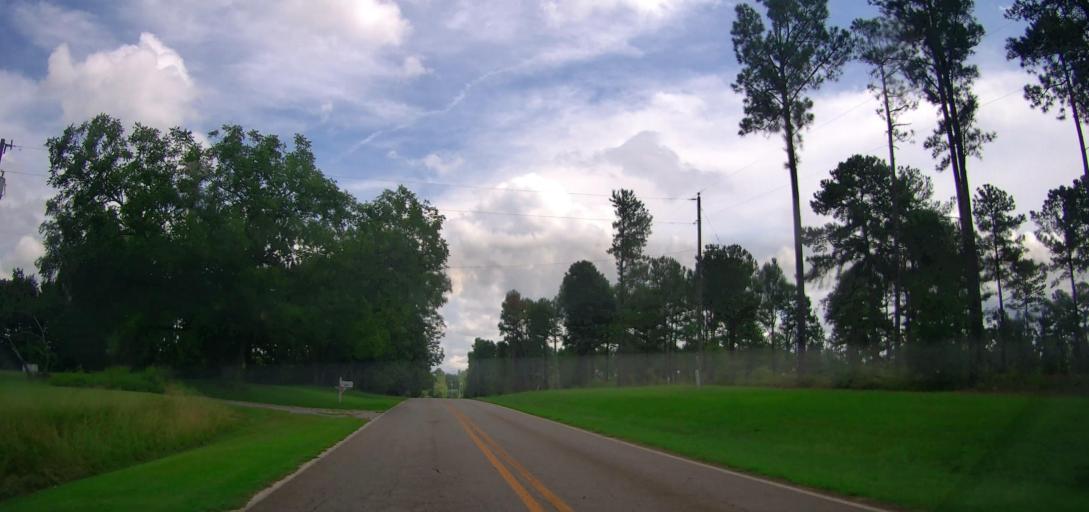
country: US
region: Georgia
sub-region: Houston County
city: Perry
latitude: 32.5221
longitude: -83.7547
